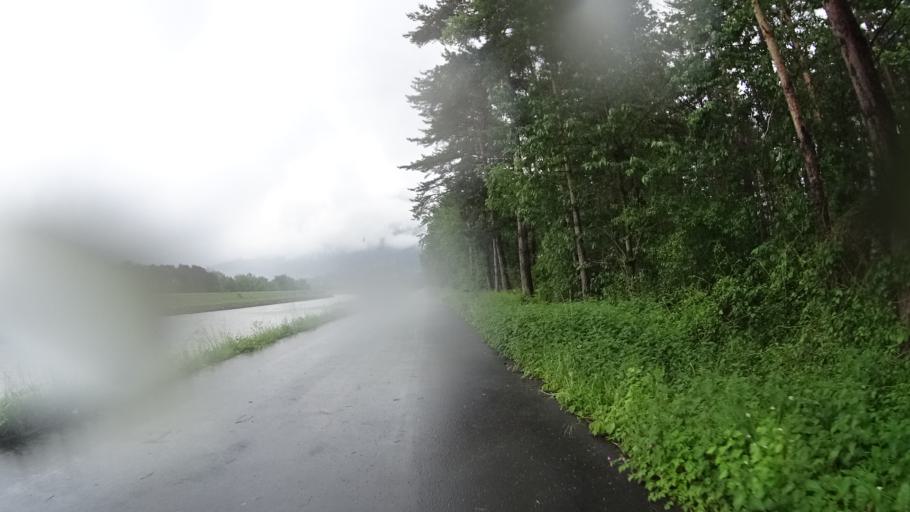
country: LI
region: Balzers
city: Balzers
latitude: 47.0807
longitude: 9.5064
